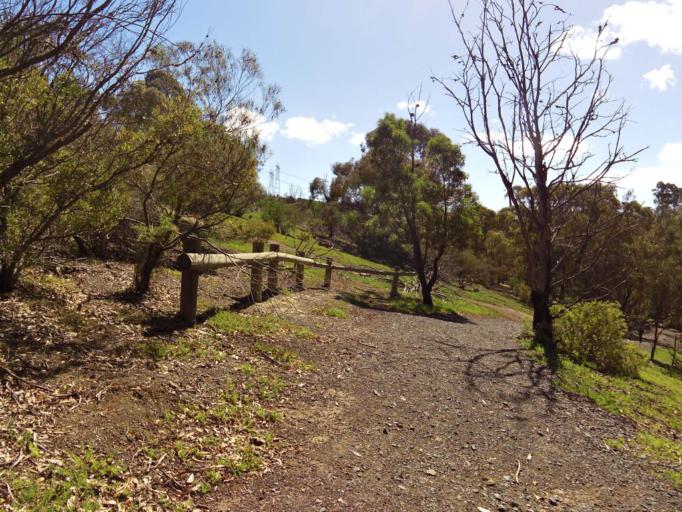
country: AU
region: Victoria
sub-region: Brimbank
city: Sydenham
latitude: -37.6651
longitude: 144.7685
